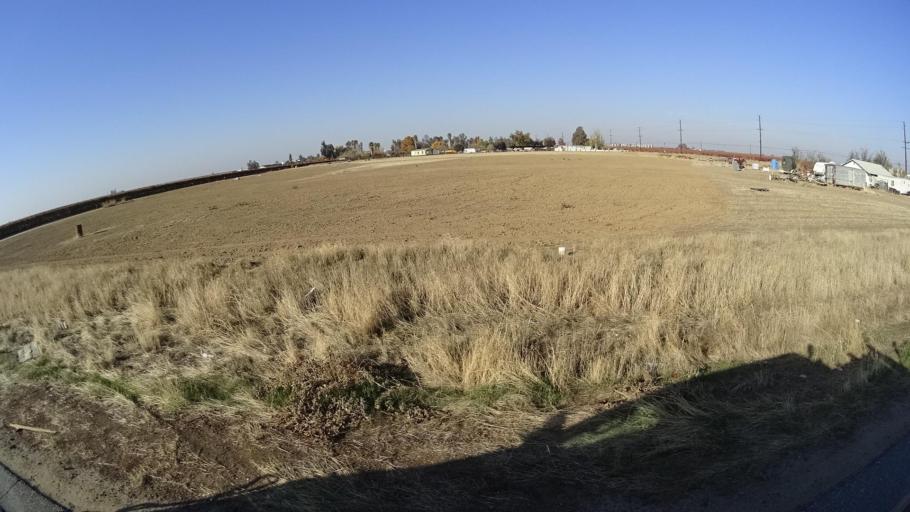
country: US
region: California
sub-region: Tulare County
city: Richgrove
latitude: 35.7749
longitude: -119.1696
